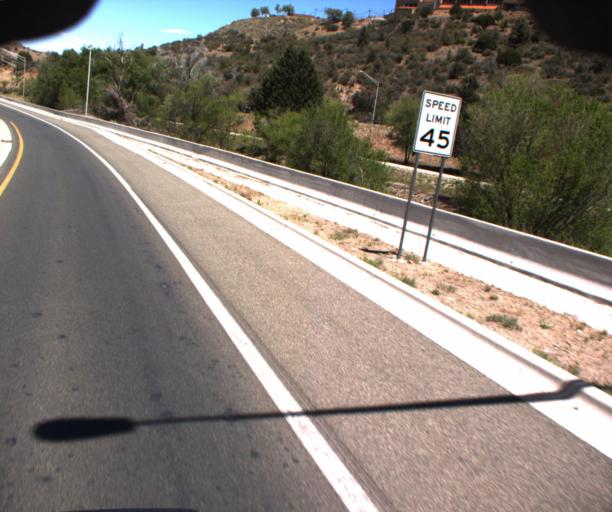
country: US
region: Arizona
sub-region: Yavapai County
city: Prescott
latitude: 34.5487
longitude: -112.4495
